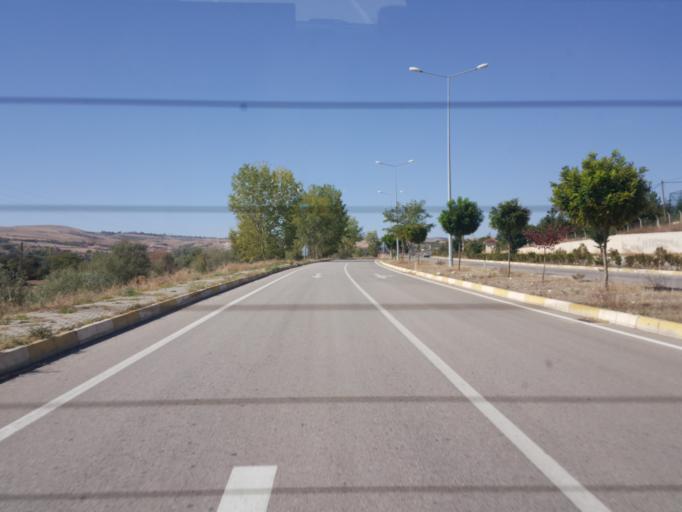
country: TR
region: Tokat
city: Zile
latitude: 40.2796
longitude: 35.8540
